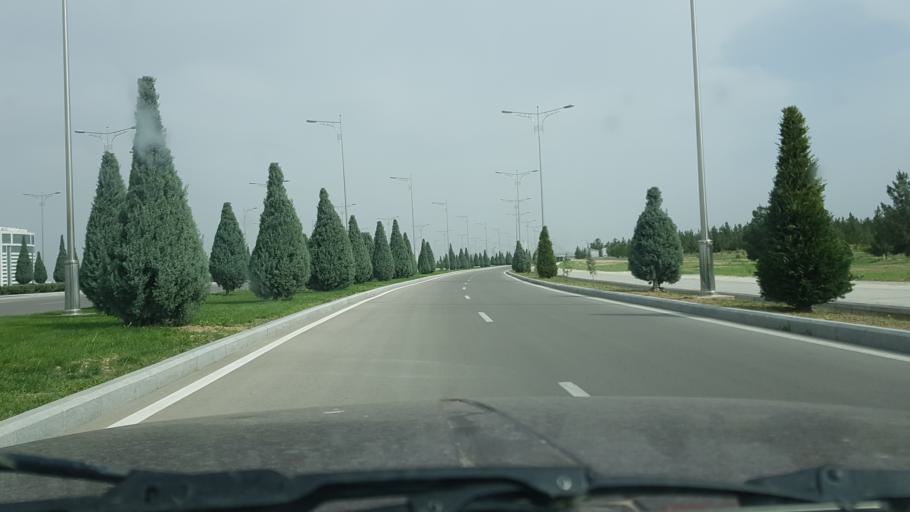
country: TM
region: Ahal
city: Ashgabat
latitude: 37.8883
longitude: 58.3353
